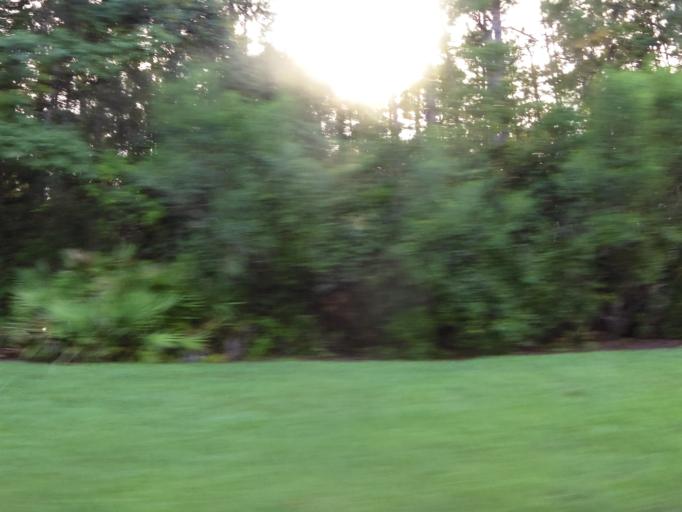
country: US
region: Florida
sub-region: Saint Johns County
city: Fruit Cove
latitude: 30.2140
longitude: -81.5395
